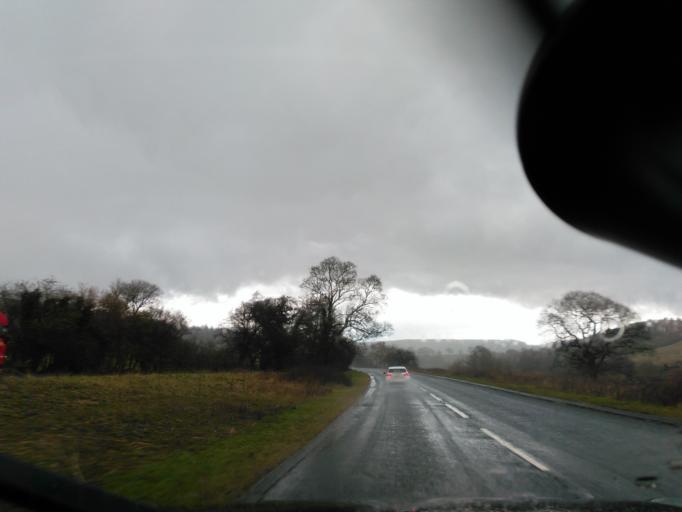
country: GB
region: England
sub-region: Bradford
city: Addingham
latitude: 53.9758
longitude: -1.9274
